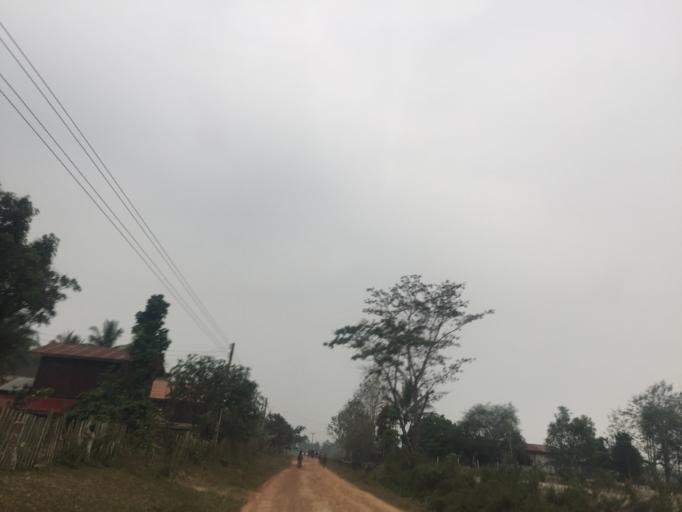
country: LA
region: Xiagnabouli
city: Sainyabuli
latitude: 19.0056
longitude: 101.5107
